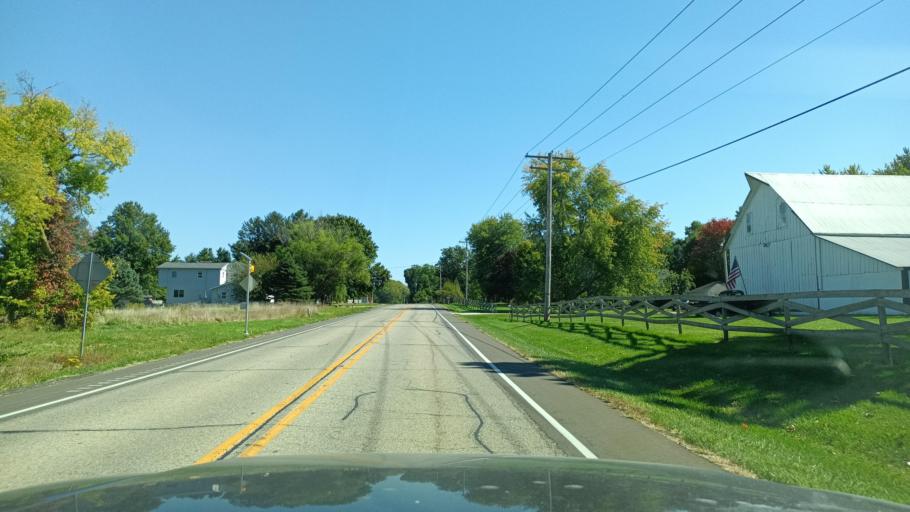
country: US
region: Illinois
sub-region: Woodford County
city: Eureka
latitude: 40.6273
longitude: -89.2584
